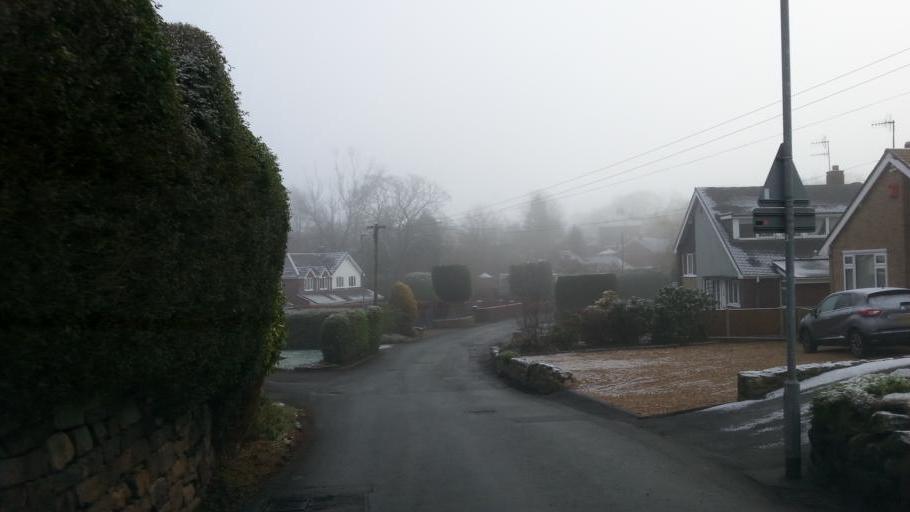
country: GB
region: England
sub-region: Staffordshire
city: Biddulph
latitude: 53.1241
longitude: -2.1726
